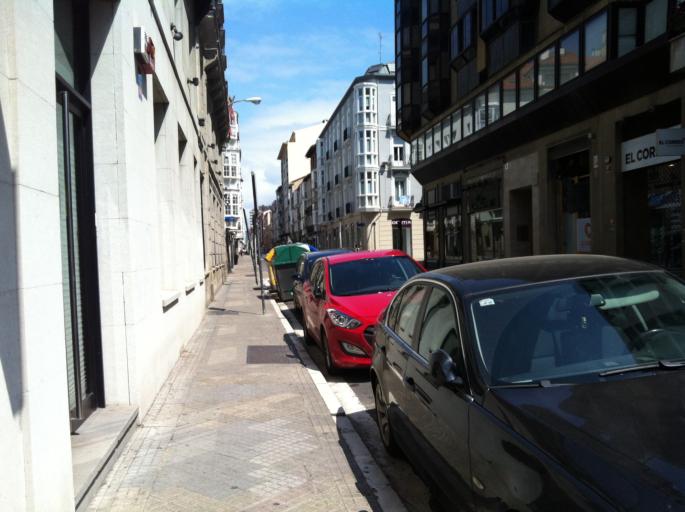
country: ES
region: Basque Country
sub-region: Provincia de Alava
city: Gasteiz / Vitoria
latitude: 42.8431
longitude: -2.6736
